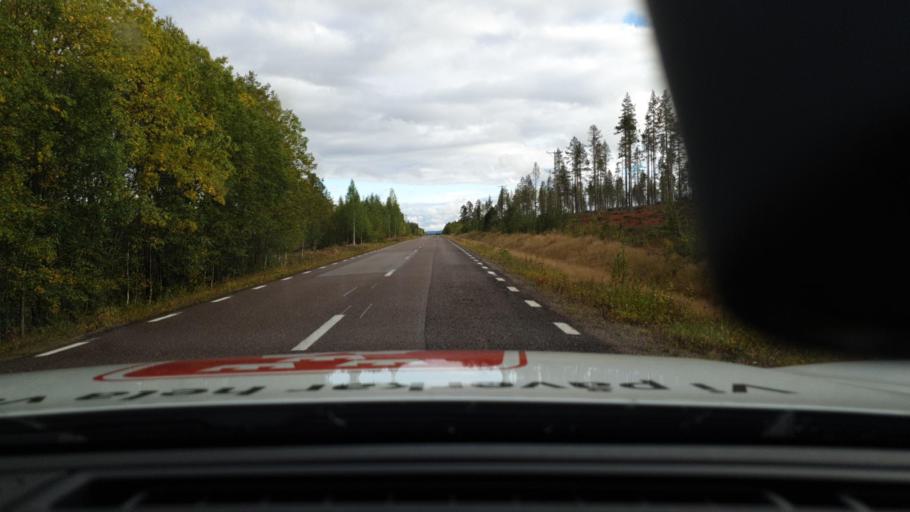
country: SE
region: Norrbotten
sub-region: Overkalix Kommun
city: OEverkalix
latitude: 67.0254
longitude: 22.5148
